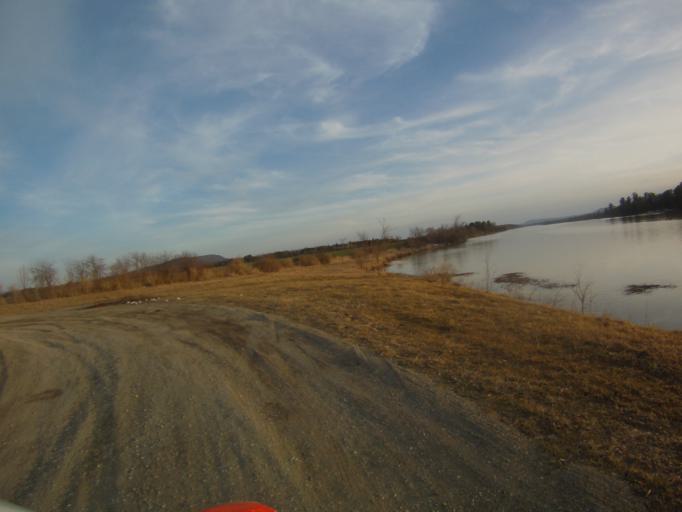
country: US
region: Vermont
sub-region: Addison County
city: Vergennes
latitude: 44.1251
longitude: -73.3295
